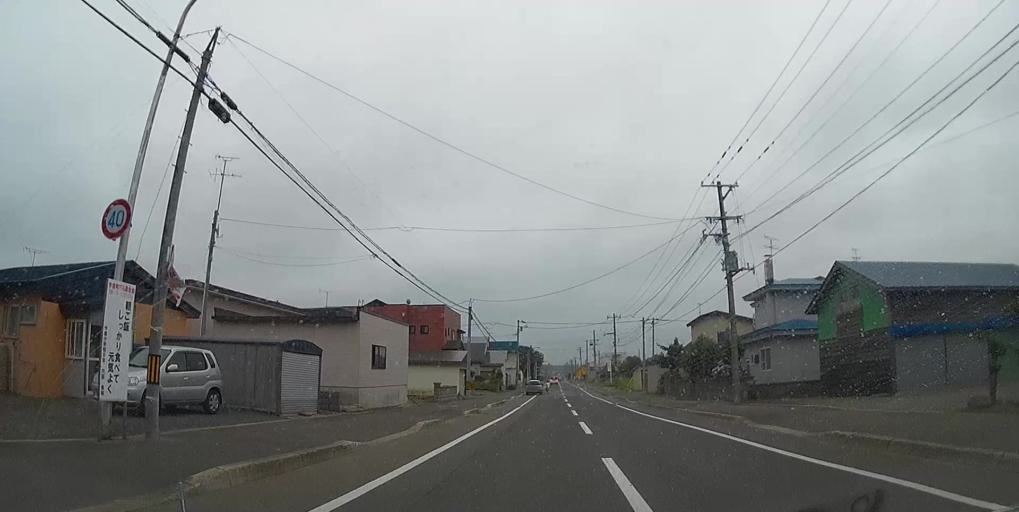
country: JP
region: Hokkaido
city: Iwanai
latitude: 42.4274
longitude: 140.0197
